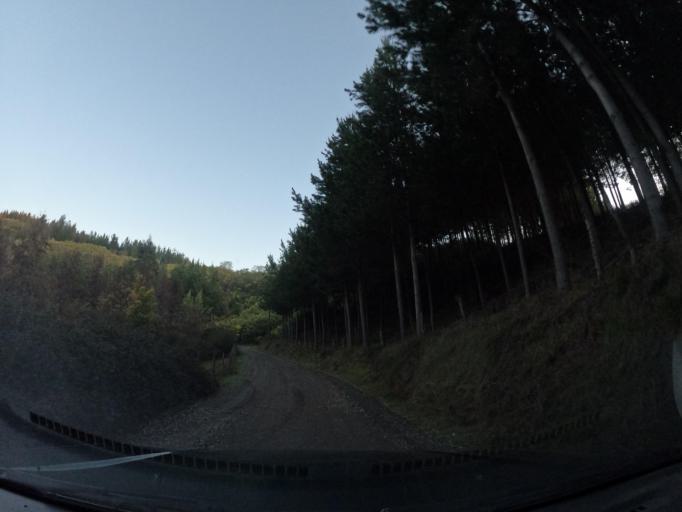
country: CL
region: Biobio
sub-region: Provincia de Concepcion
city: Chiguayante
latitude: -36.9940
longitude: -72.8333
